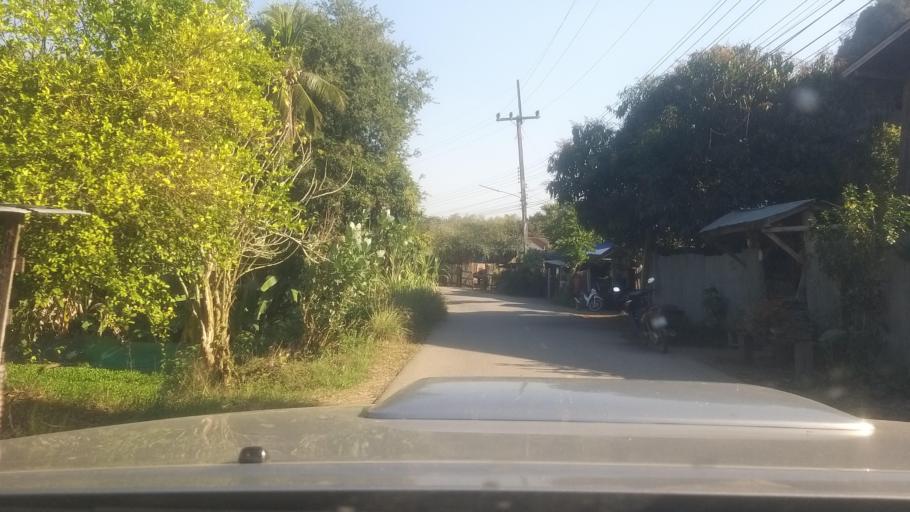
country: TH
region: Phrae
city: Phrae
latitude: 18.2617
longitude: 99.9934
